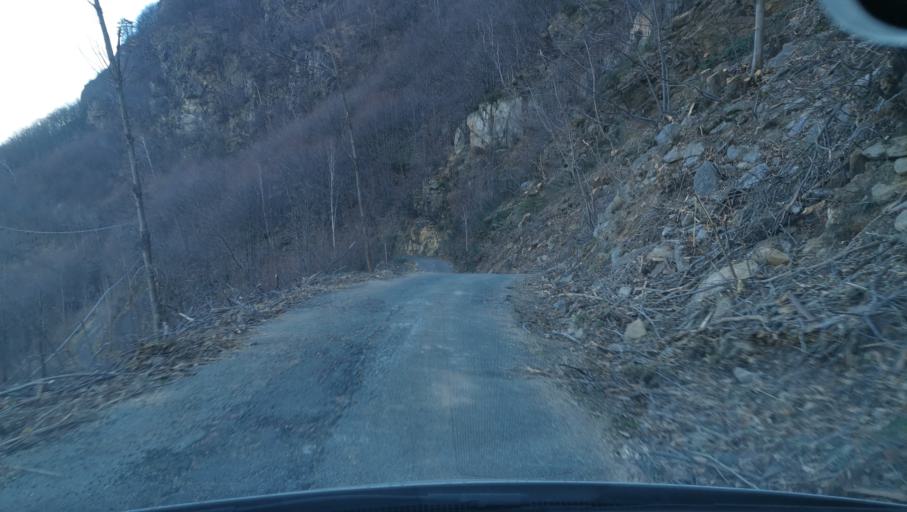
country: IT
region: Piedmont
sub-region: Provincia di Torino
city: Tavagnasco
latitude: 45.5400
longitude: 7.8165
